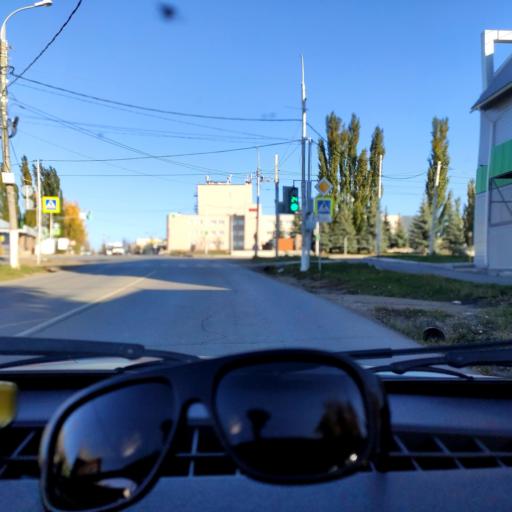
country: RU
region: Bashkortostan
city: Blagoveshchensk
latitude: 55.0452
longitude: 55.9593
